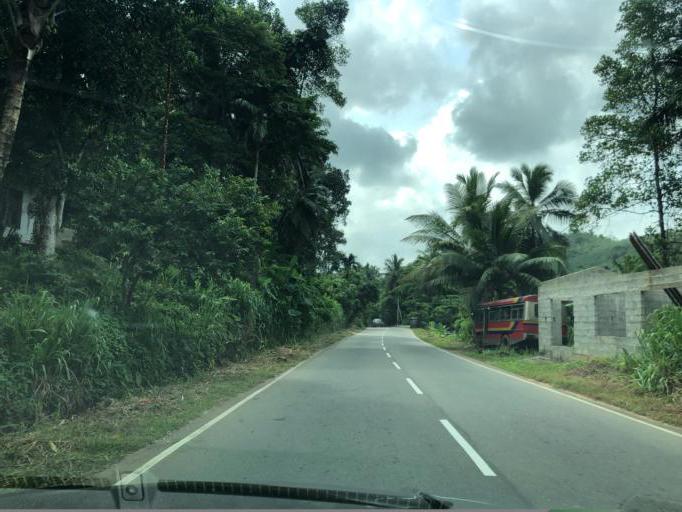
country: LK
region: Western
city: Horana South
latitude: 6.6898
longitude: 80.1428
